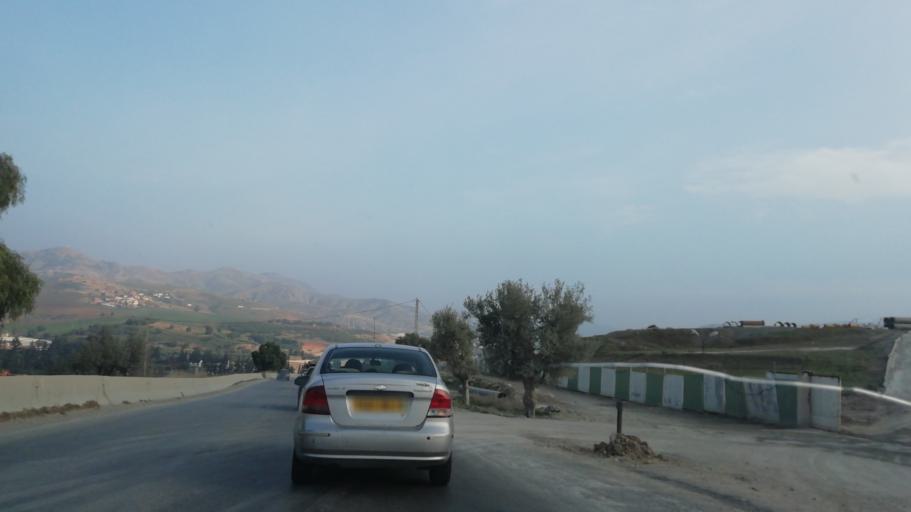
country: DZ
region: Mascara
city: Bou Hanifia el Hamamat
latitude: 35.4714
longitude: -0.0144
